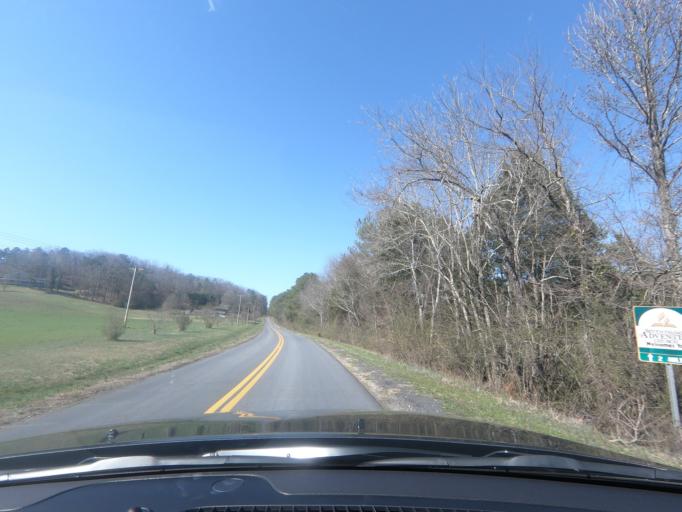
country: US
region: Georgia
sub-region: Gordon County
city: Calhoun
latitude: 34.4617
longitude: -84.9852
